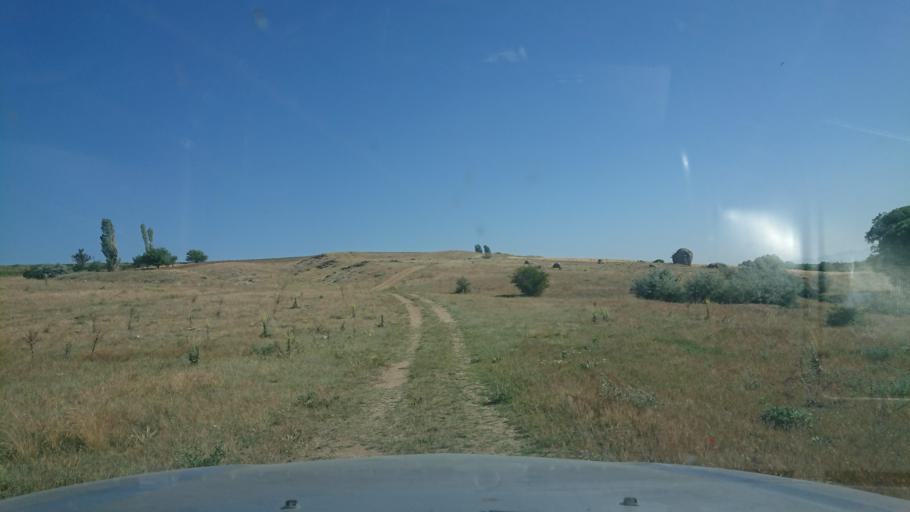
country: TR
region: Aksaray
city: Agacoren
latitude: 38.8452
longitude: 33.9267
